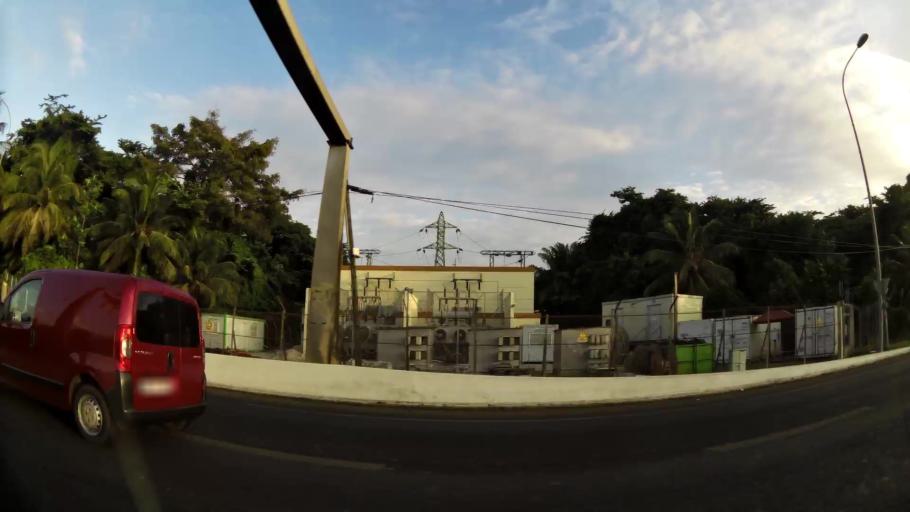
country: GP
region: Guadeloupe
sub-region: Guadeloupe
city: Pointe-a-Pitre
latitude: 16.2540
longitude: -61.5373
